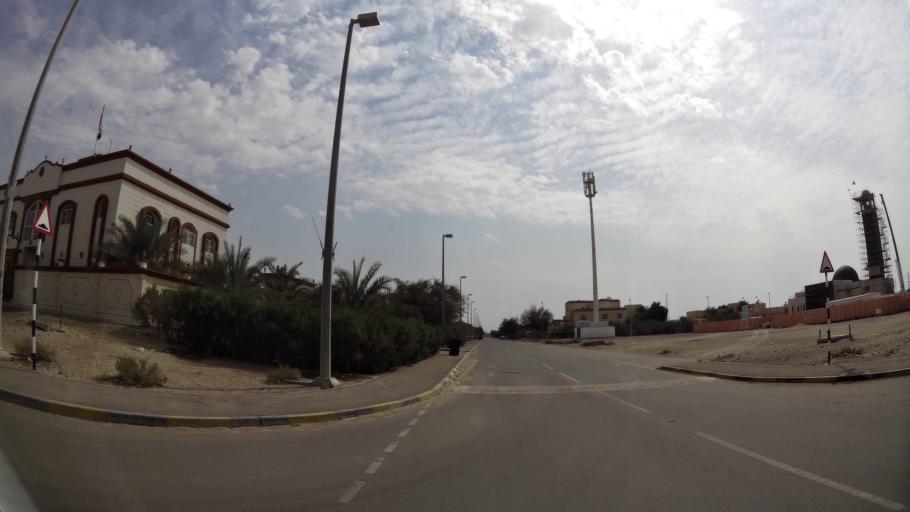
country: AE
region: Abu Dhabi
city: Abu Dhabi
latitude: 24.5577
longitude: 54.6906
